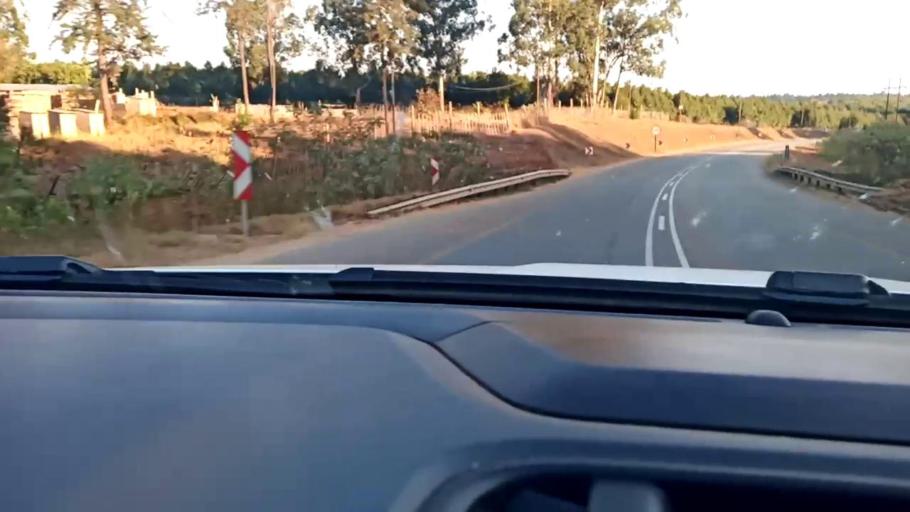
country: ZA
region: Limpopo
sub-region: Mopani District Municipality
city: Duiwelskloof
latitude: -23.7100
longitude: 30.1298
